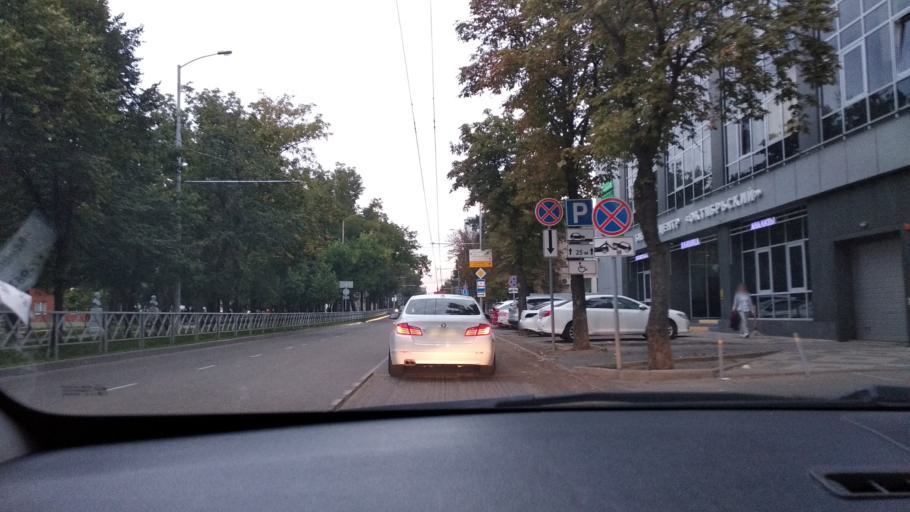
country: RU
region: Adygeya
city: Yablonovskiy
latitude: 45.0139
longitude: 38.9625
